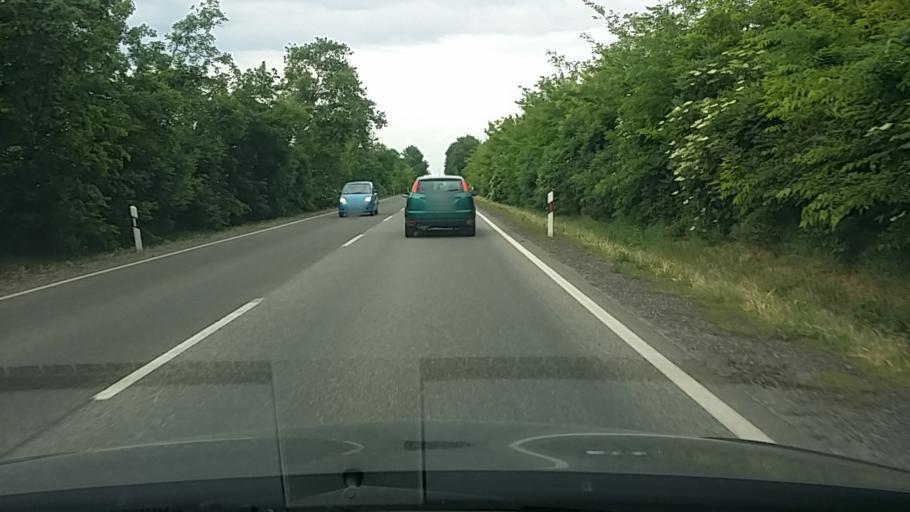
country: HU
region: Fejer
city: dunaujvaros
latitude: 46.9514
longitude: 18.9124
